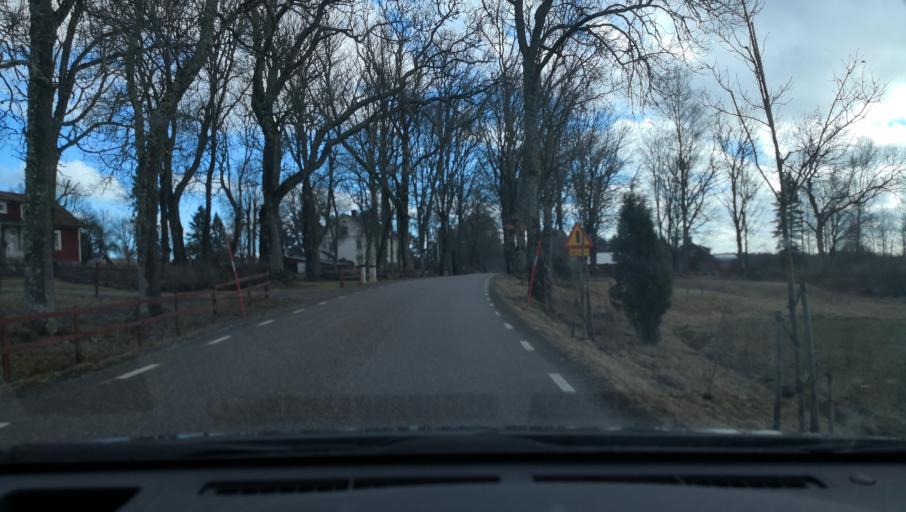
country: SE
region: OErebro
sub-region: Lindesbergs Kommun
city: Fellingsbro
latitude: 59.3474
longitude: 15.6861
